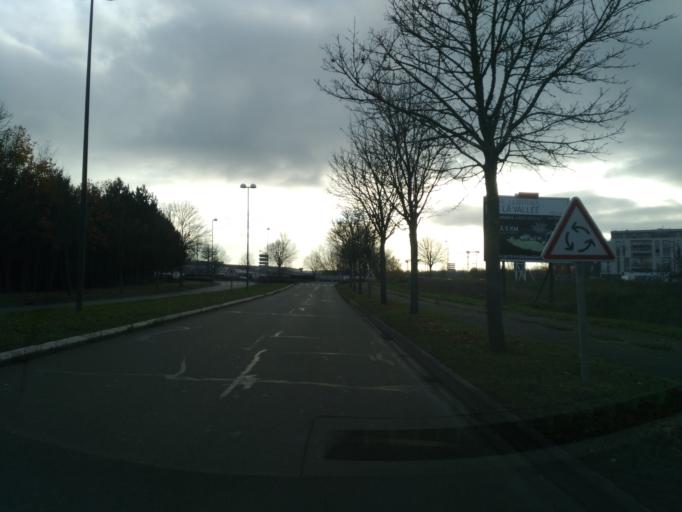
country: FR
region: Ile-de-France
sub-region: Departement des Yvelines
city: Guyancourt
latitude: 48.7672
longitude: 2.0808
